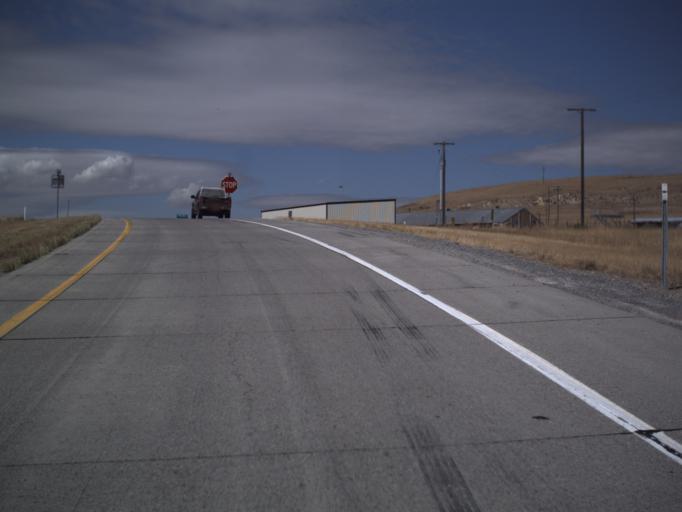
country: US
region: Utah
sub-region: Box Elder County
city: Tremonton
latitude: 41.7205
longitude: -112.2268
